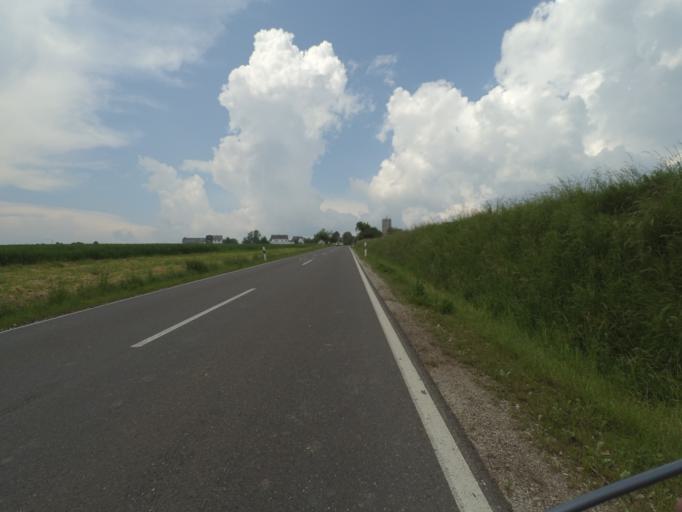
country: DE
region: Rheinland-Pfalz
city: Beltheim
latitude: 50.1013
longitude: 7.4629
